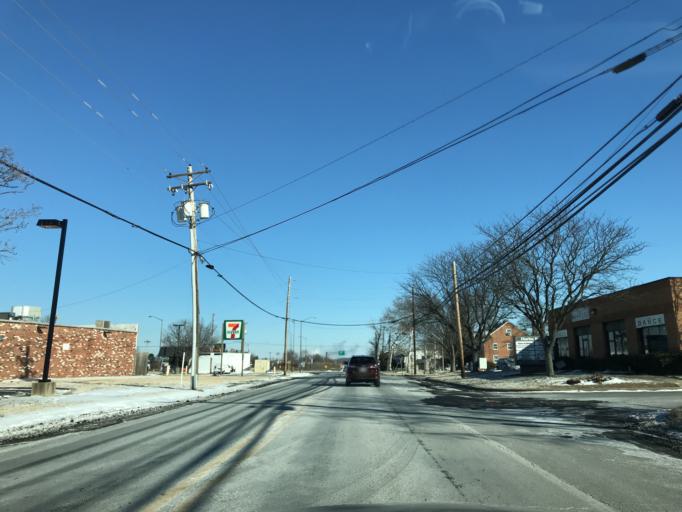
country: US
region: Maryland
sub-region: Prince George's County
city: Brandywine
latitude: 38.6508
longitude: -76.8818
